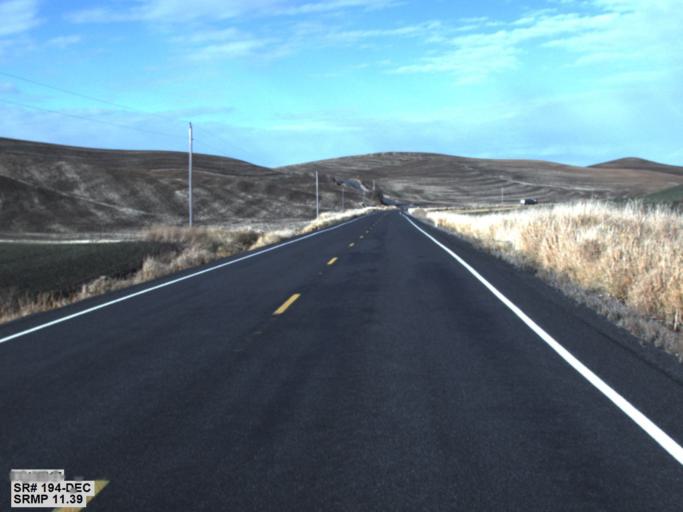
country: US
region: Washington
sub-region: Whitman County
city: Colfax
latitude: 46.7508
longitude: -117.3709
